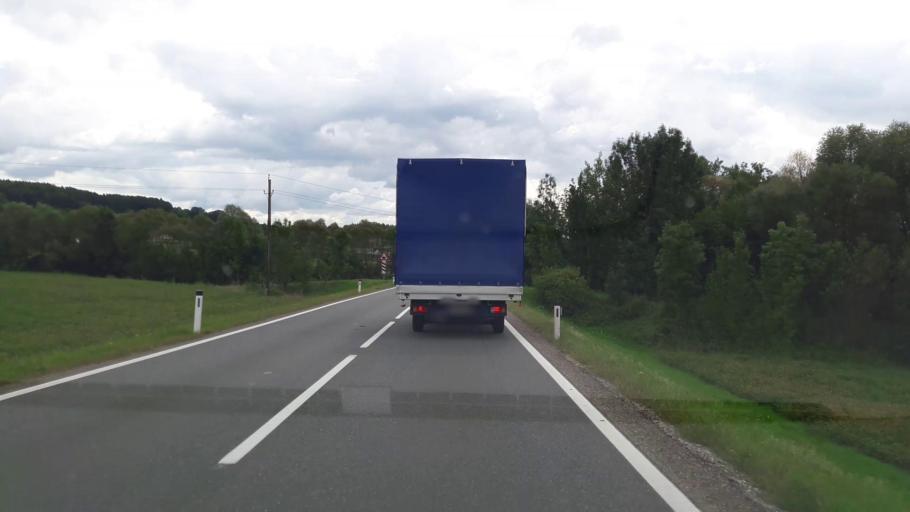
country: AT
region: Styria
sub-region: Politischer Bezirk Weiz
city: Sankt Ruprecht an der Raab
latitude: 47.1594
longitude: 15.6653
